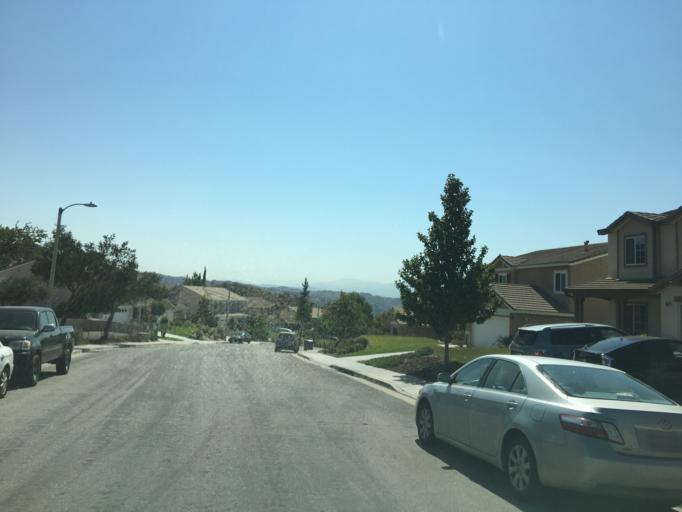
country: US
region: California
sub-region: Los Angeles County
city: Castaic
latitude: 34.4742
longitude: -118.6350
